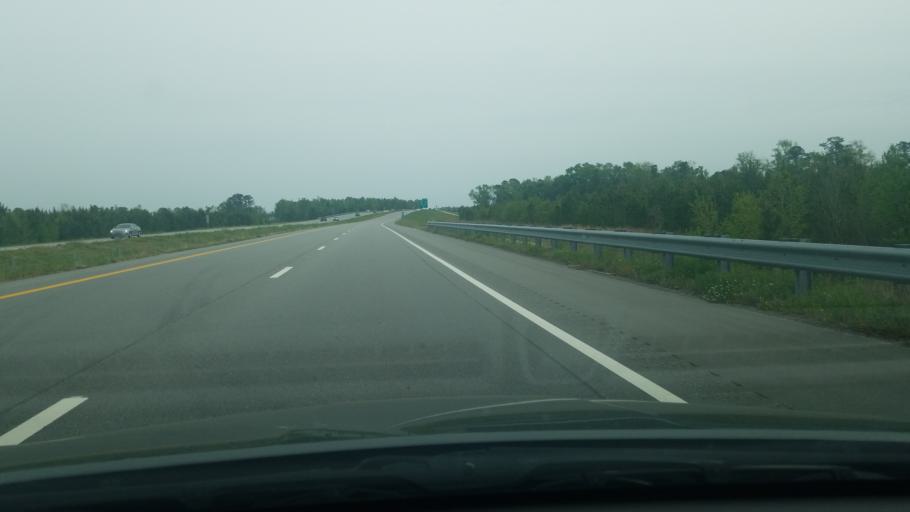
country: US
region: North Carolina
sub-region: Jones County
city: Maysville
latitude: 34.9942
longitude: -77.2346
